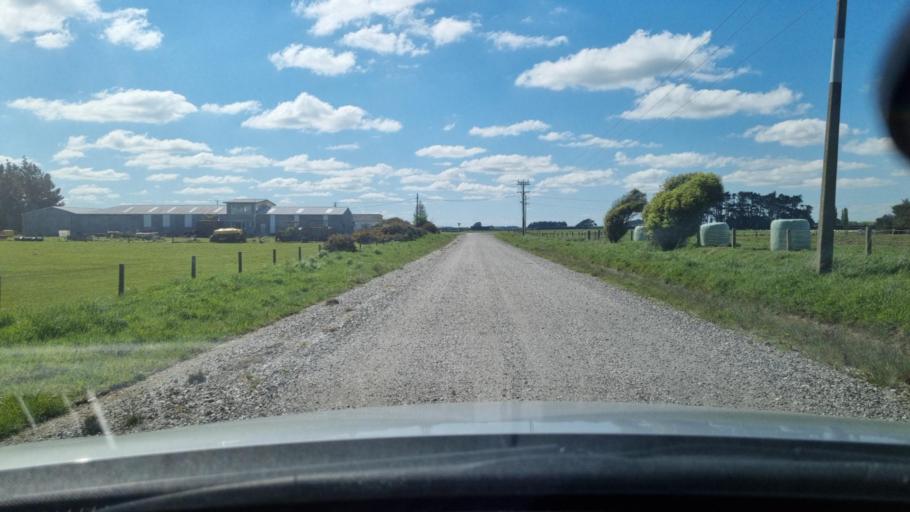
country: NZ
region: Southland
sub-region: Invercargill City
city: Invercargill
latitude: -46.3711
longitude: 168.2985
